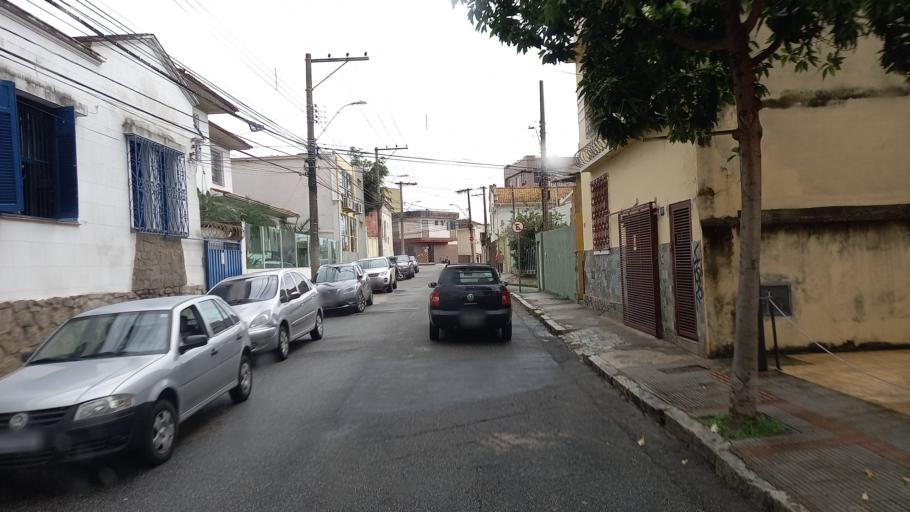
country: BR
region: Minas Gerais
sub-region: Belo Horizonte
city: Belo Horizonte
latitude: -19.9109
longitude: -43.9289
